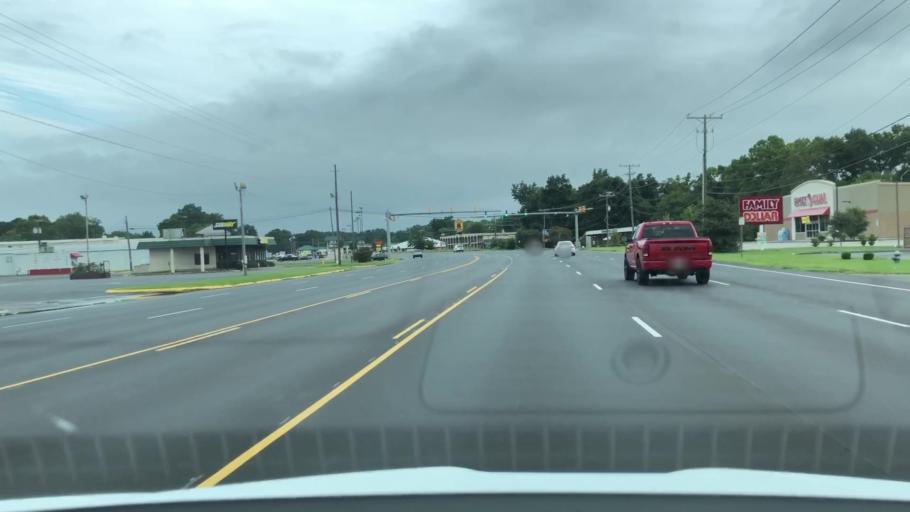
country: US
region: North Carolina
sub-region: Lenoir County
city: Kinston
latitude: 35.2414
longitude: -77.5780
